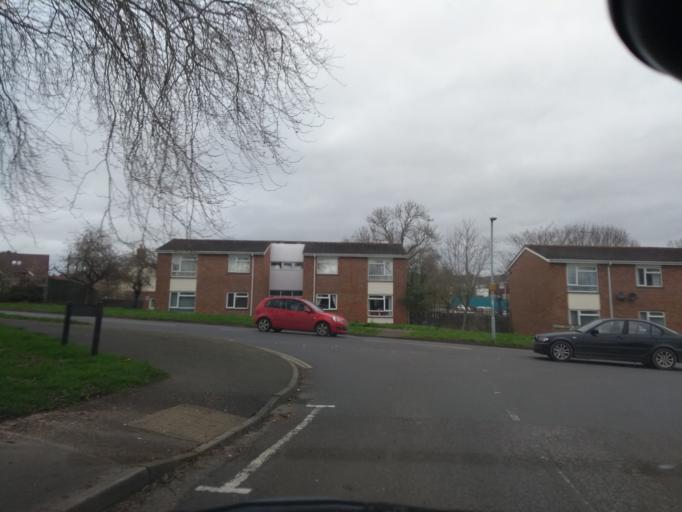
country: GB
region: England
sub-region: Somerset
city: Taunton
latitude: 51.0321
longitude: -3.0953
